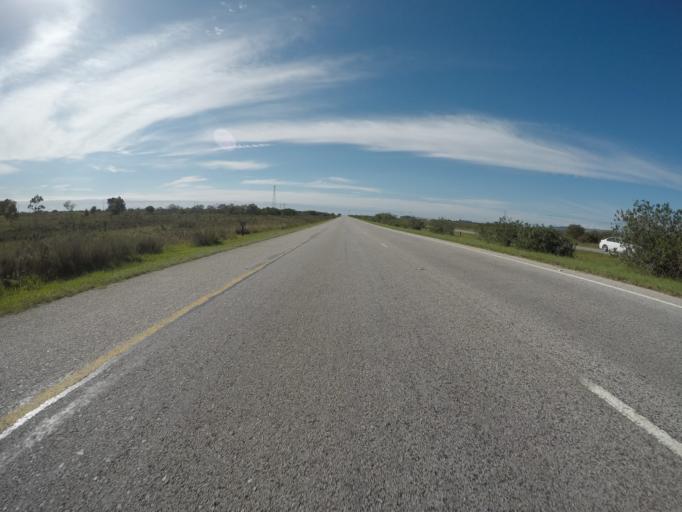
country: ZA
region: Eastern Cape
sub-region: Nelson Mandela Bay Metropolitan Municipality
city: Port Elizabeth
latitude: -33.9489
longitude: 25.4438
